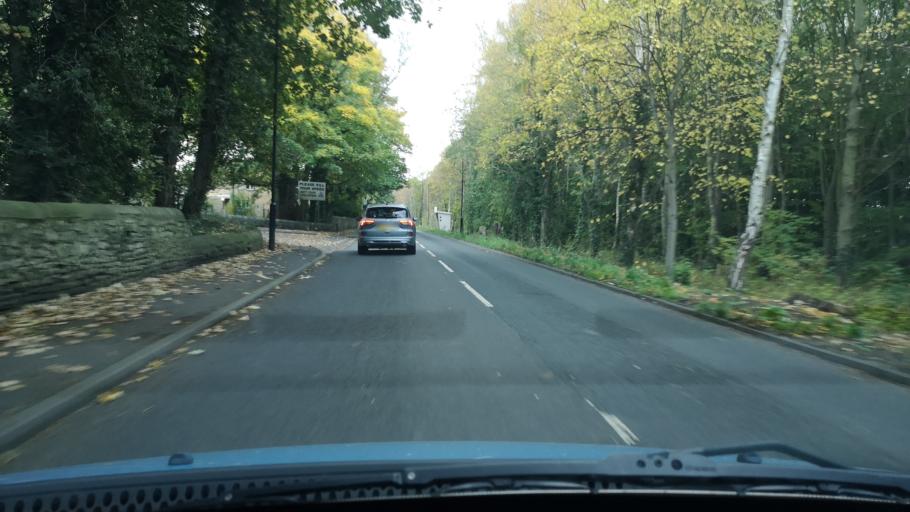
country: GB
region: England
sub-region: Doncaster
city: Campsall
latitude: 53.6203
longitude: -1.1685
